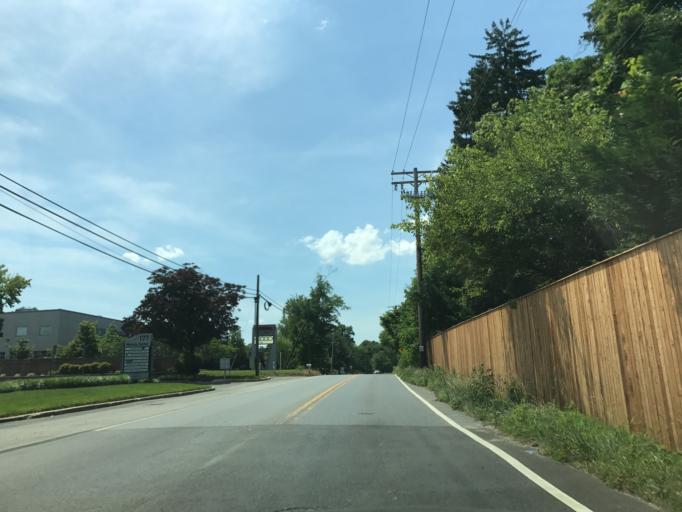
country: US
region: Maryland
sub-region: Anne Arundel County
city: Parole
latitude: 38.9854
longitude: -76.5587
